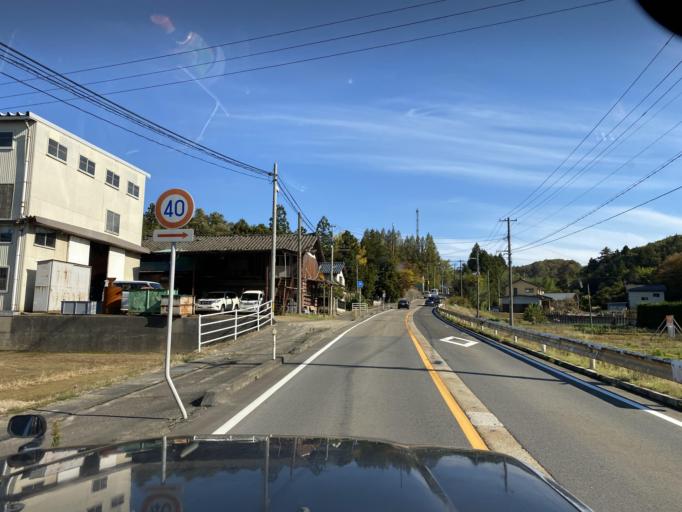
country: JP
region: Niigata
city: Niitsu-honcho
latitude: 37.7508
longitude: 139.1007
